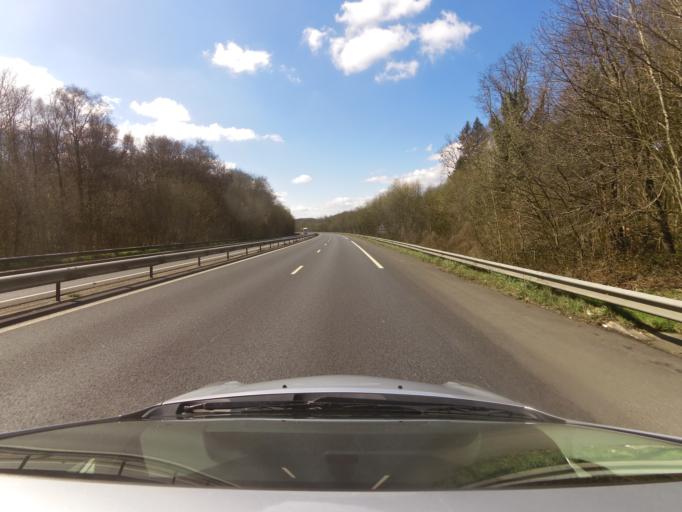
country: FR
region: Haute-Normandie
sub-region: Departement de la Seine-Maritime
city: Saint-Saens
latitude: 49.6733
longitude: 1.3223
